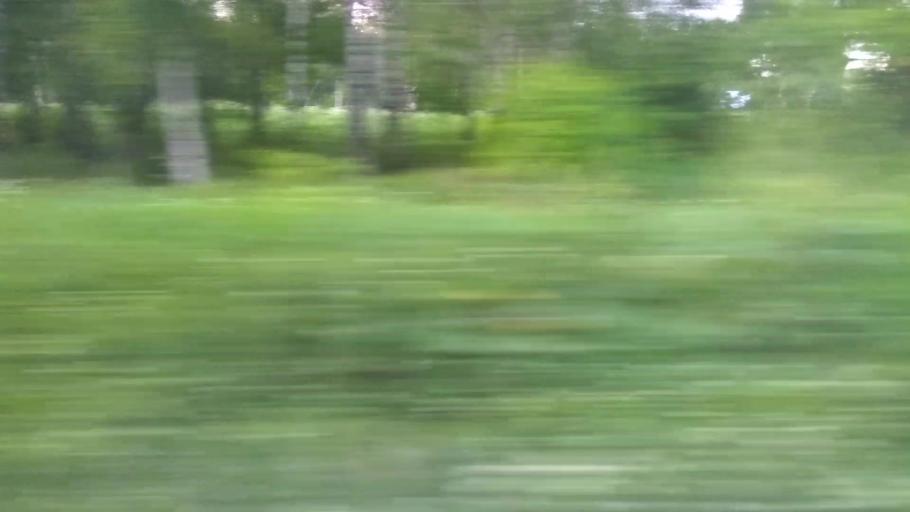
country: RU
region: Moskovskaya
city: Barybino
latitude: 55.2808
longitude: 37.8918
